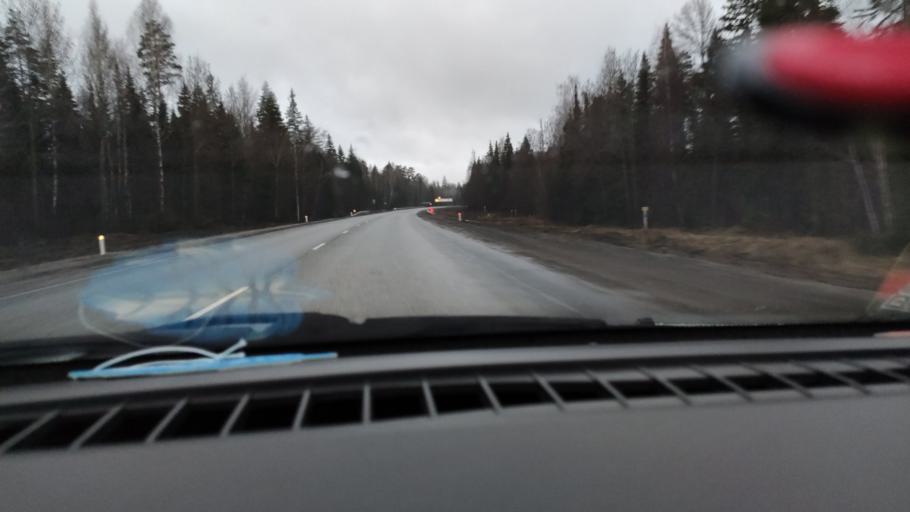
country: RU
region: Udmurtiya
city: Alnashi
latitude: 56.0909
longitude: 52.4446
